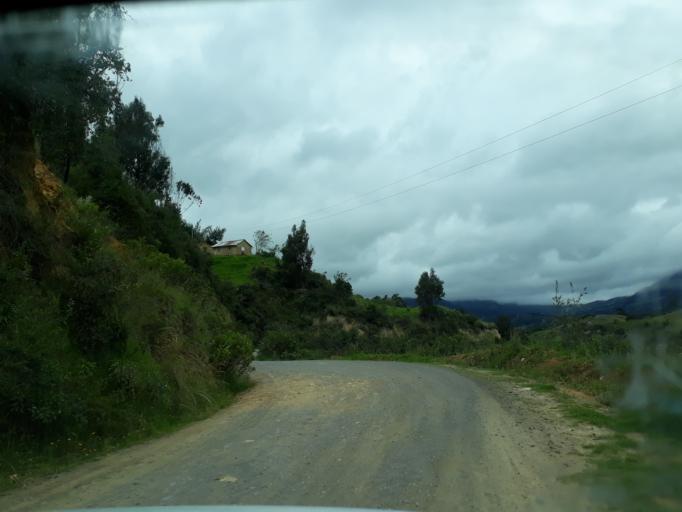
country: CO
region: Cundinamarca
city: Carmen de Carupa
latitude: 5.3182
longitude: -73.8919
